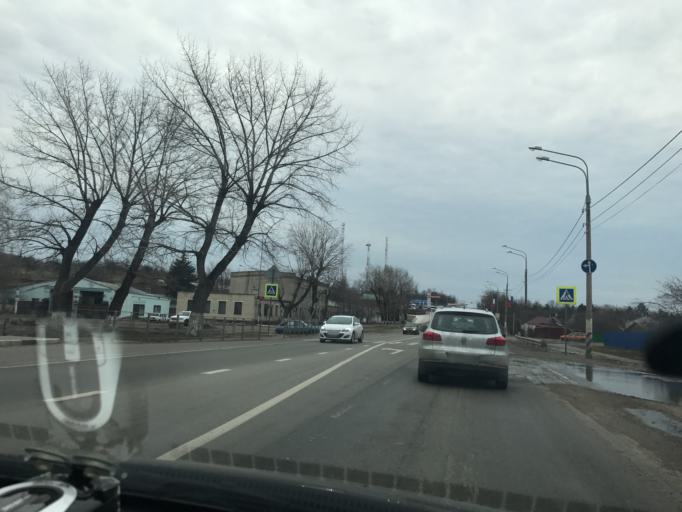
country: RU
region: Krasnodarskiy
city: Kropotkin
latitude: 45.4272
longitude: 40.5386
